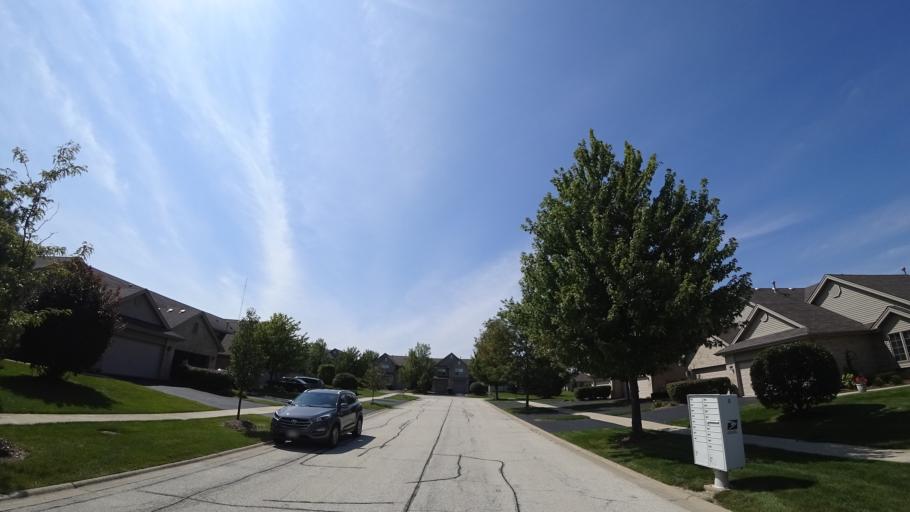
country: US
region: Illinois
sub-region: Cook County
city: Orland Hills
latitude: 41.5593
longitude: -87.8413
